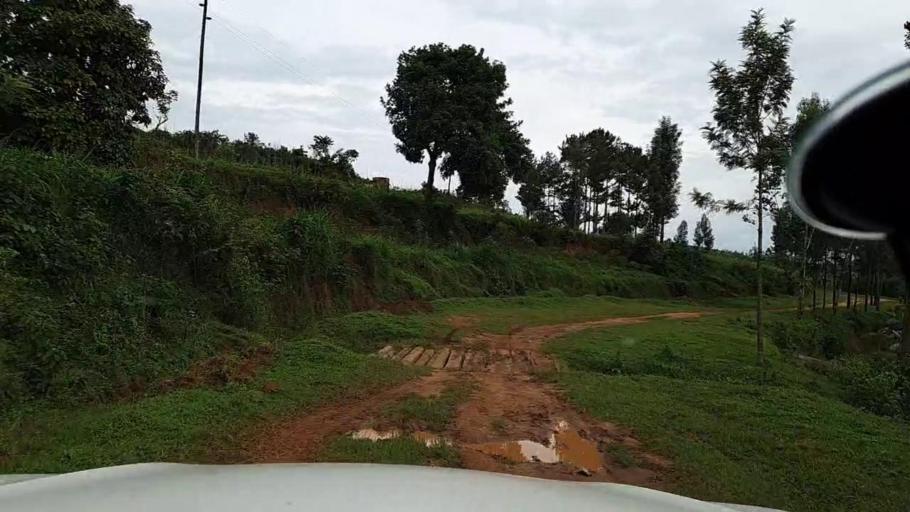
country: RW
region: Southern Province
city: Gitarama
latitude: -2.1166
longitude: 29.6459
